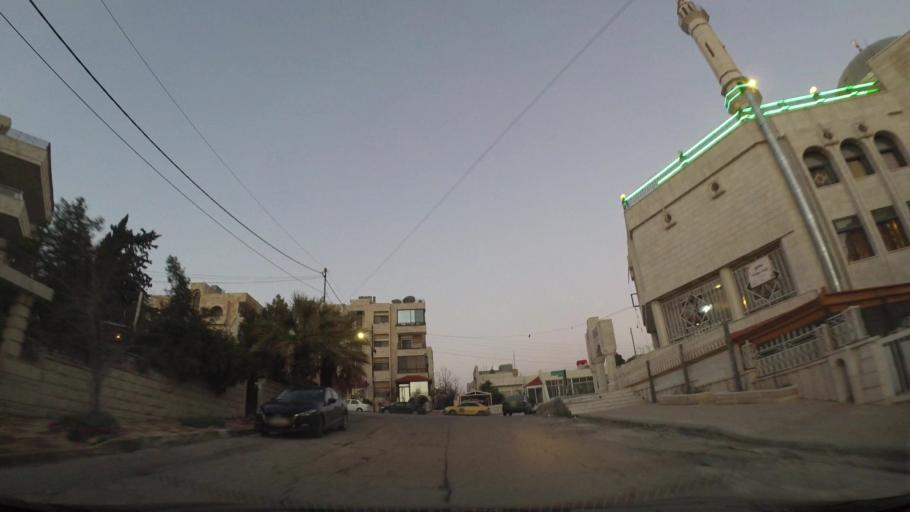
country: JO
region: Amman
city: Al Jubayhah
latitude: 31.9851
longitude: 35.8909
